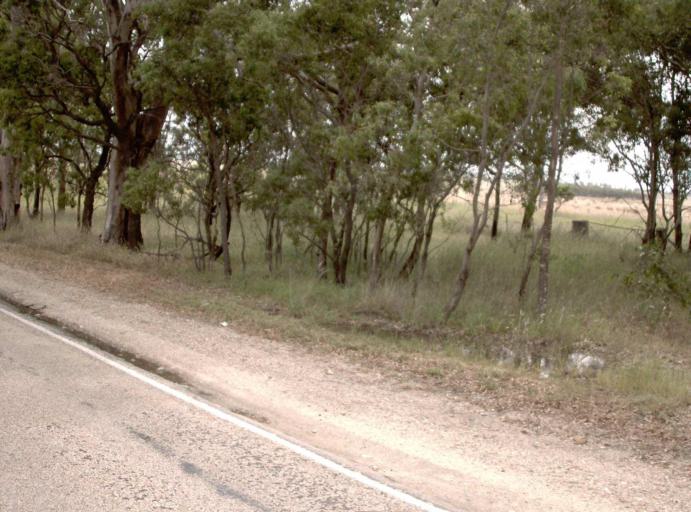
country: AU
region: Victoria
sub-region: Wellington
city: Sale
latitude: -37.9353
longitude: 147.0959
